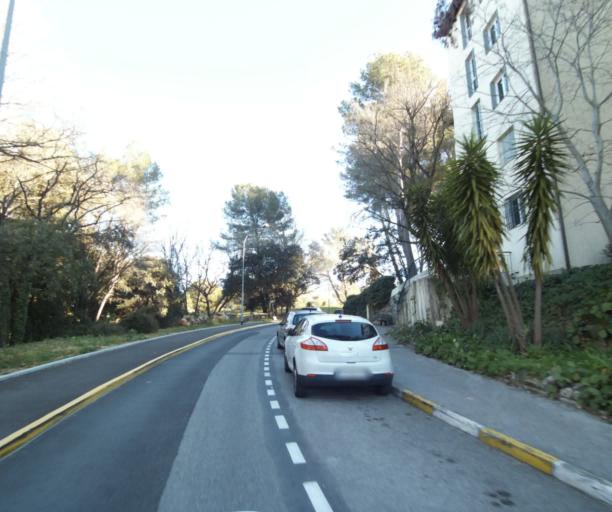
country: FR
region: Provence-Alpes-Cote d'Azur
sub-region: Departement des Alpes-Maritimes
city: Vallauris
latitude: 43.5969
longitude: 7.0662
